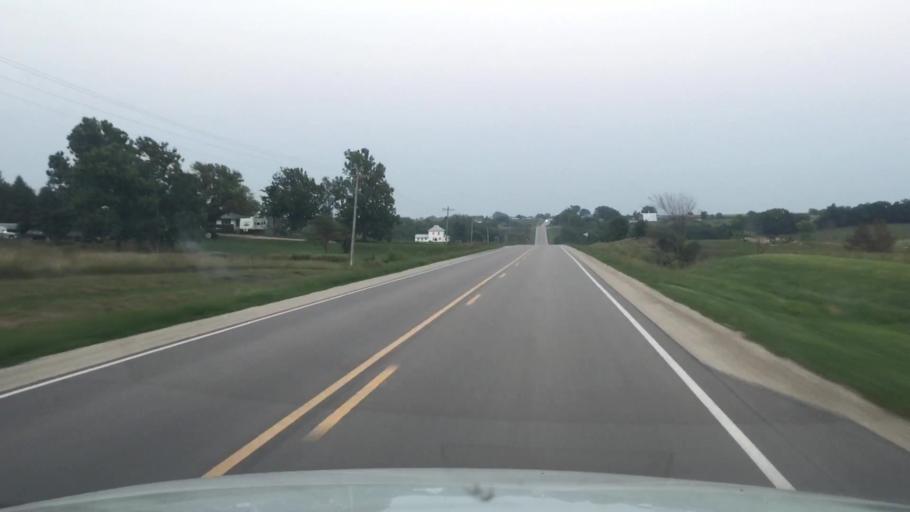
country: US
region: Iowa
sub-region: Warren County
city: Indianola
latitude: 41.1825
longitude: -93.4722
